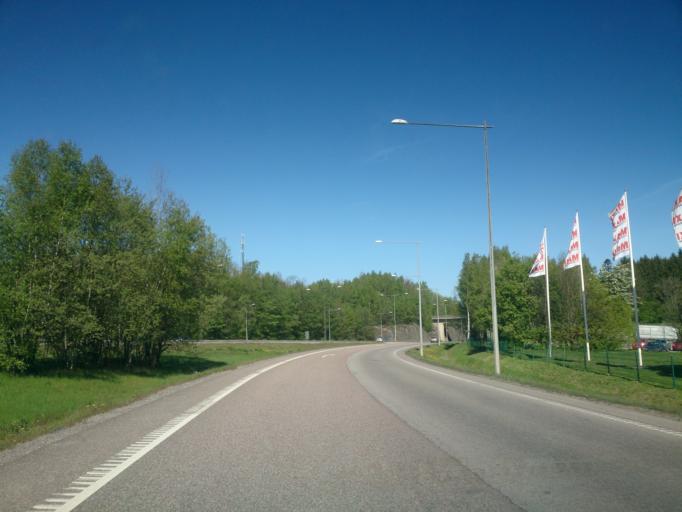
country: SE
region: Stockholm
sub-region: Haninge Kommun
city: Haninge
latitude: 59.1803
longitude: 18.1563
